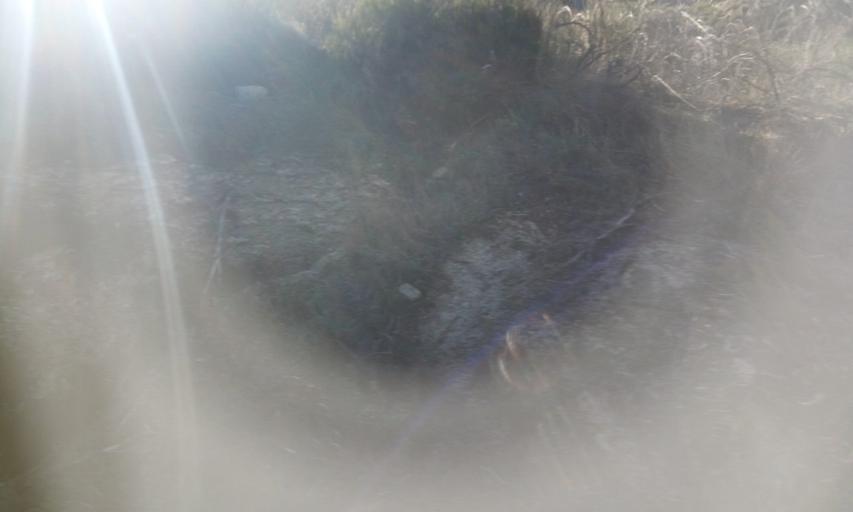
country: PT
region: Guarda
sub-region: Manteigas
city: Manteigas
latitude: 40.4847
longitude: -7.5172
